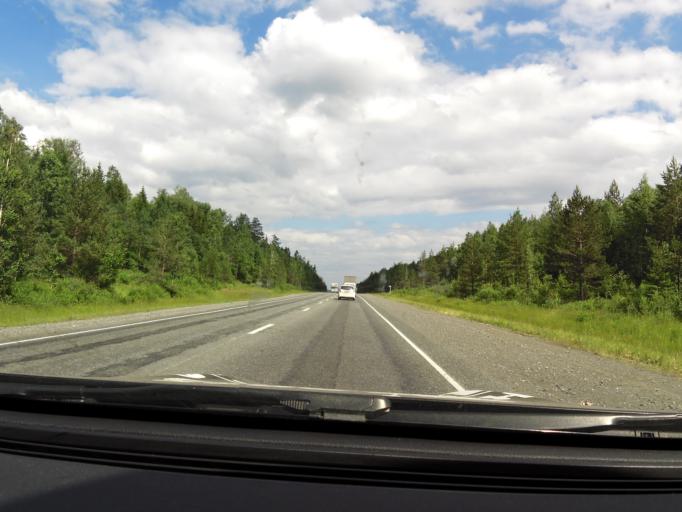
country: RU
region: Sverdlovsk
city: Nizhniye Sergi
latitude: 56.8251
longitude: 59.2417
